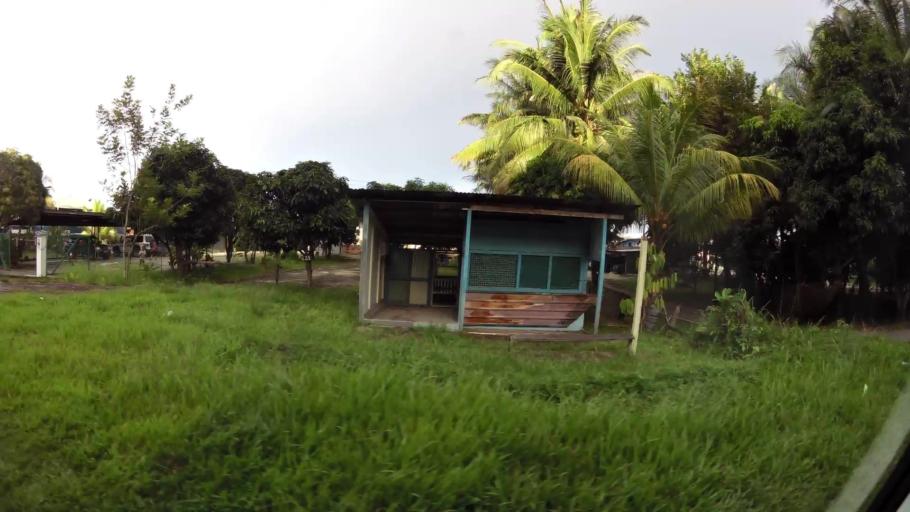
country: BN
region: Brunei and Muara
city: Bandar Seri Begawan
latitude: 4.9364
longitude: 115.0178
